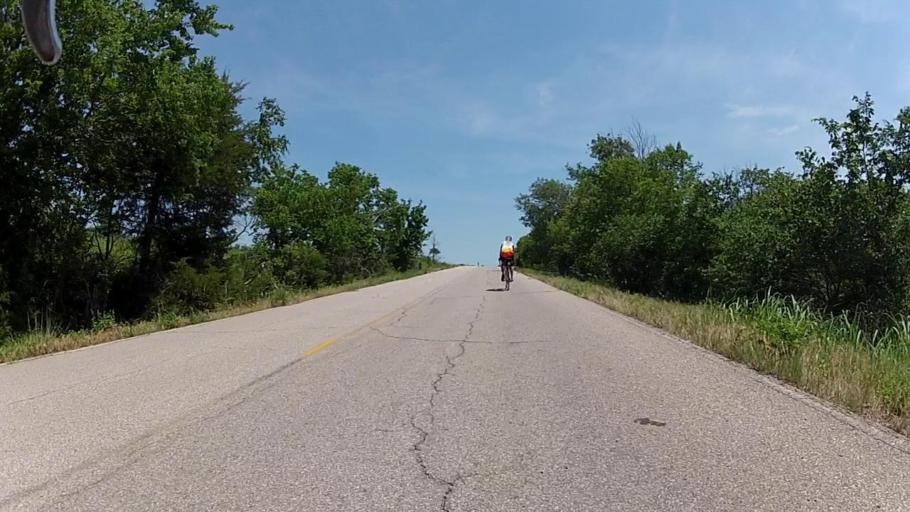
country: US
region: Kansas
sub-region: Chautauqua County
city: Sedan
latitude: 37.1089
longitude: -96.4764
